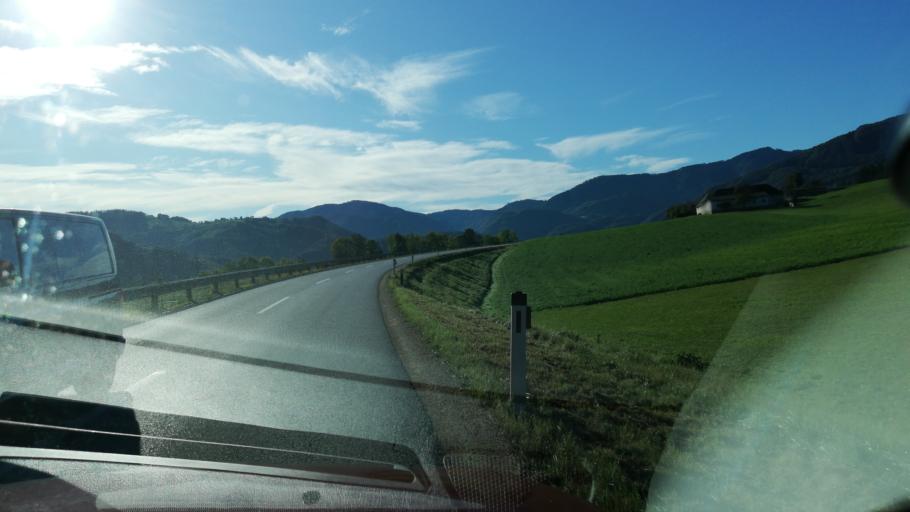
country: AT
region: Upper Austria
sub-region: Politischer Bezirk Steyr-Land
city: Ternberg
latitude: 47.9703
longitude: 14.3430
